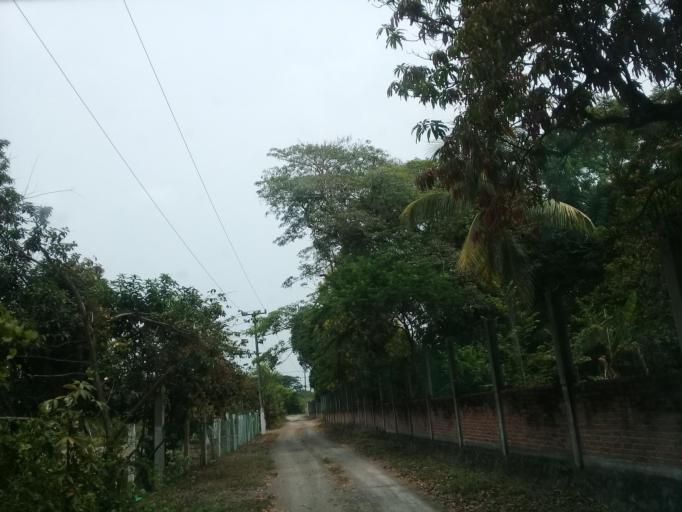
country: MX
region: Veracruz
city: El Tejar
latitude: 19.0446
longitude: -96.1944
